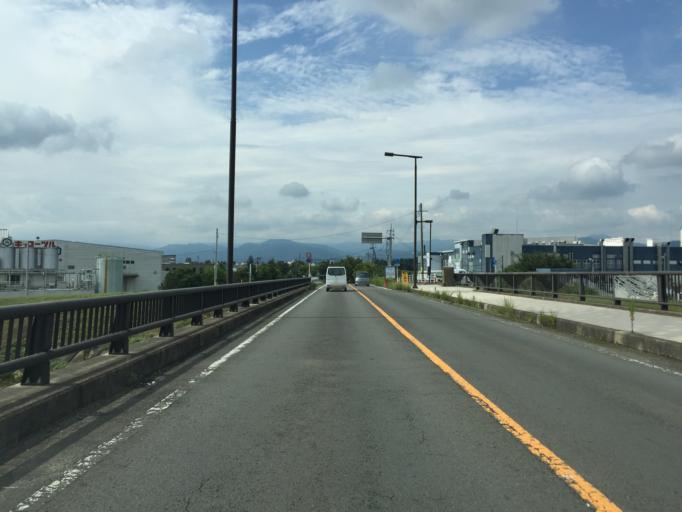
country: JP
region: Fukushima
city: Hobaramachi
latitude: 37.7984
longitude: 140.5046
